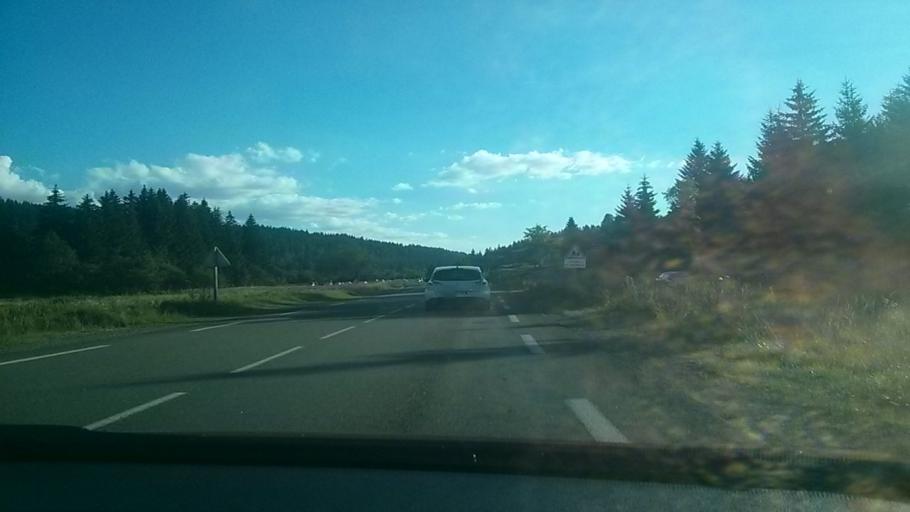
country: FR
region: Franche-Comte
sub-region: Departement du Jura
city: Longchaumois
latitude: 46.4005
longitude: 5.9852
